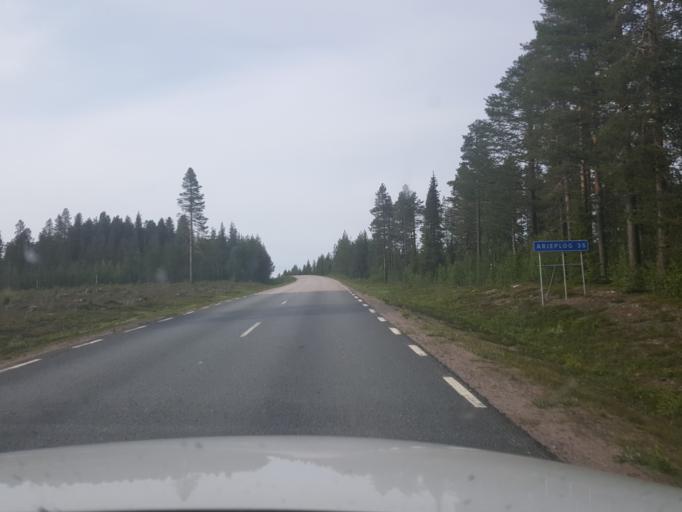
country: SE
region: Norrbotten
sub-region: Arjeplogs Kommun
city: Arjeplog
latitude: 65.7654
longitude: 18.0221
